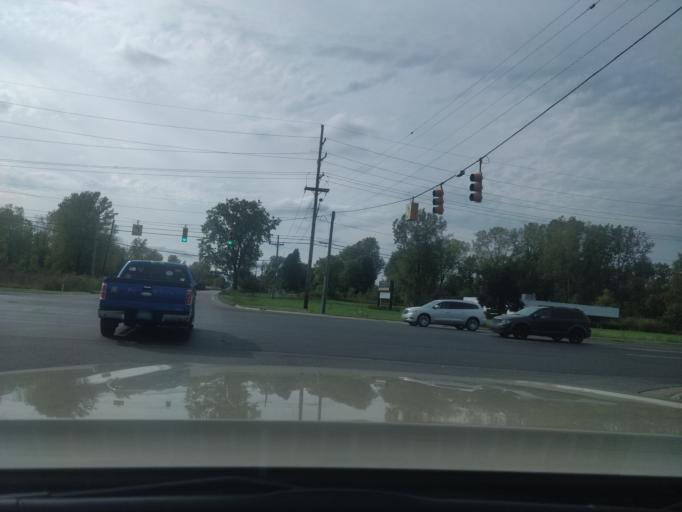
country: US
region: Michigan
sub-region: Wayne County
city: Woodhaven
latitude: 42.1526
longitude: -83.2660
